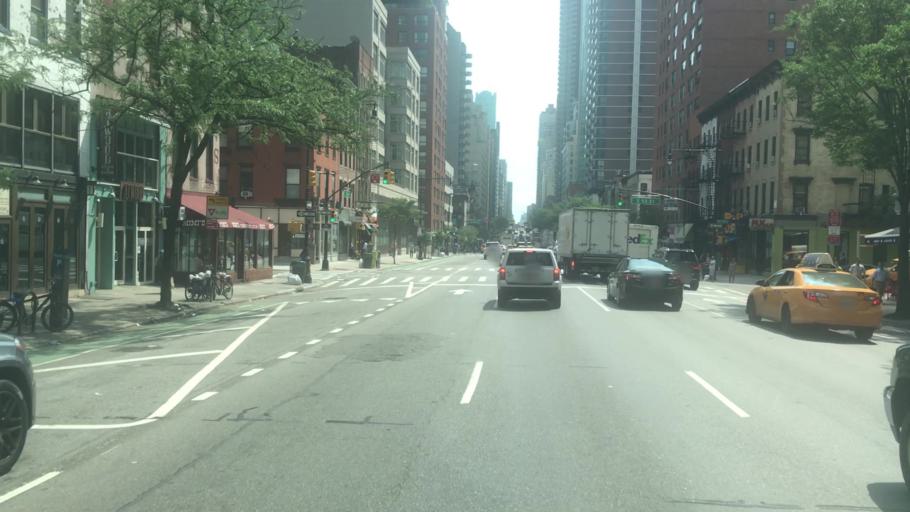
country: US
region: New York
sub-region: Queens County
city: Long Island City
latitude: 40.7565
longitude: -73.9673
